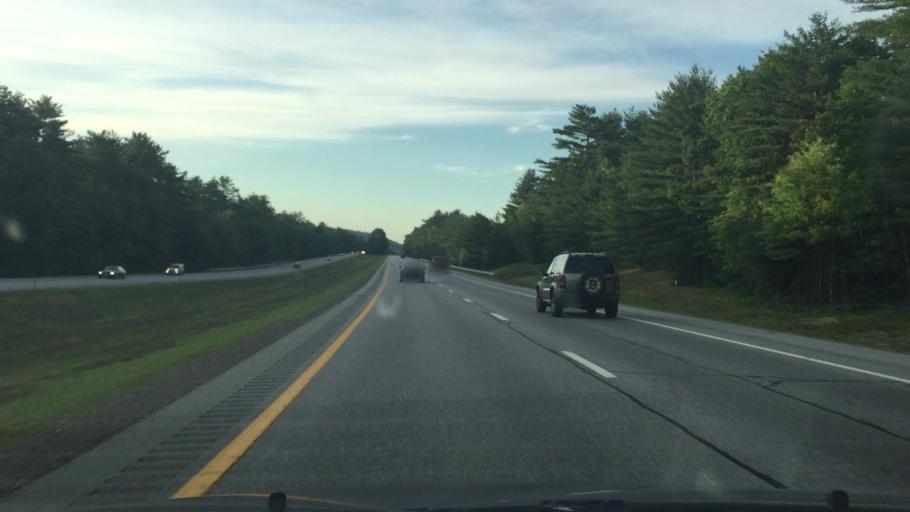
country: US
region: New Hampshire
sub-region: Grafton County
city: Ashland
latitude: 43.6474
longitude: -71.6470
